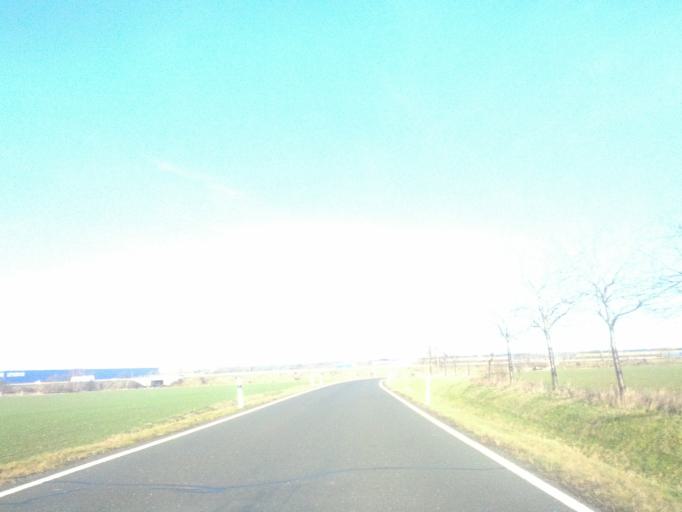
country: DE
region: Thuringia
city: Horselgau
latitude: 50.9133
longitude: 10.5720
